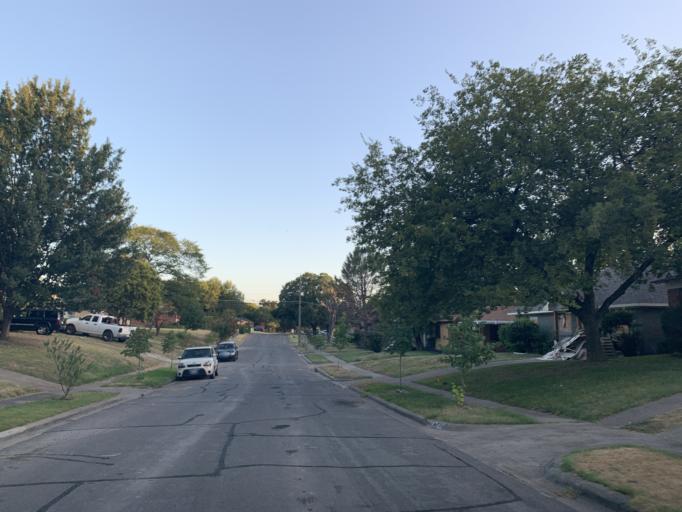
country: US
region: Texas
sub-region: Dallas County
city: Dallas
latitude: 32.6979
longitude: -96.8085
